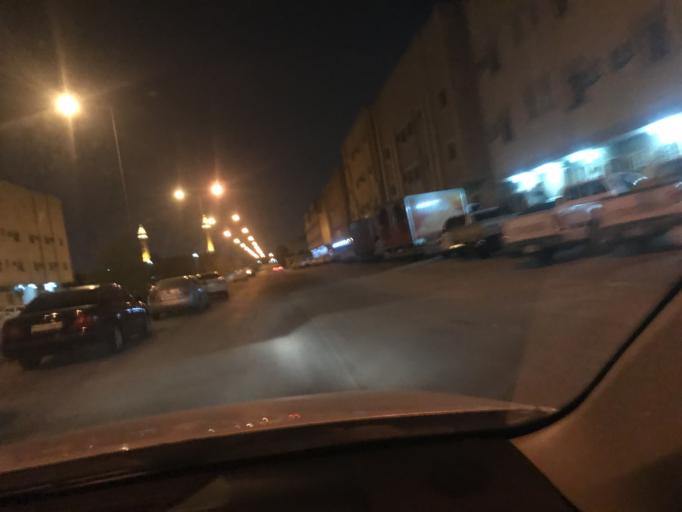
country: SA
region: Ar Riyad
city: Riyadh
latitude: 24.8192
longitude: 46.7946
